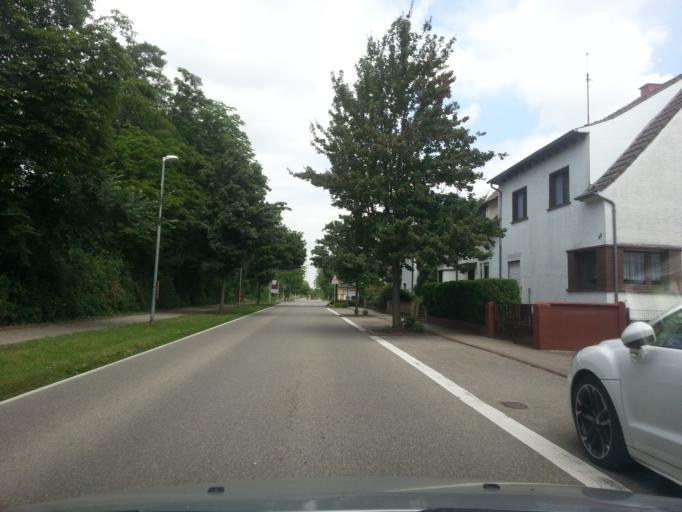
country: DE
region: Baden-Wuerttemberg
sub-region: Karlsruhe Region
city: Ketsch
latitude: 49.3737
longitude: 8.5269
